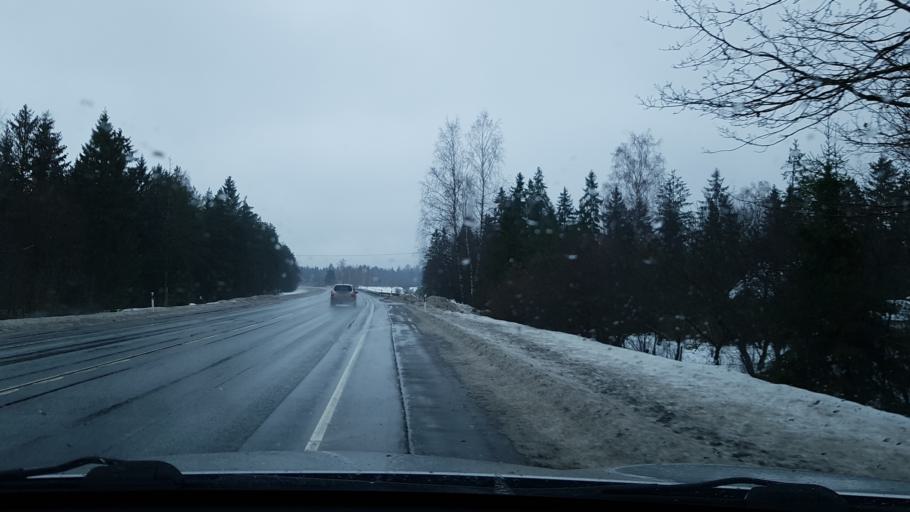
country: EE
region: Raplamaa
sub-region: Kohila vald
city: Kohila
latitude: 59.1855
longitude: 24.7855
